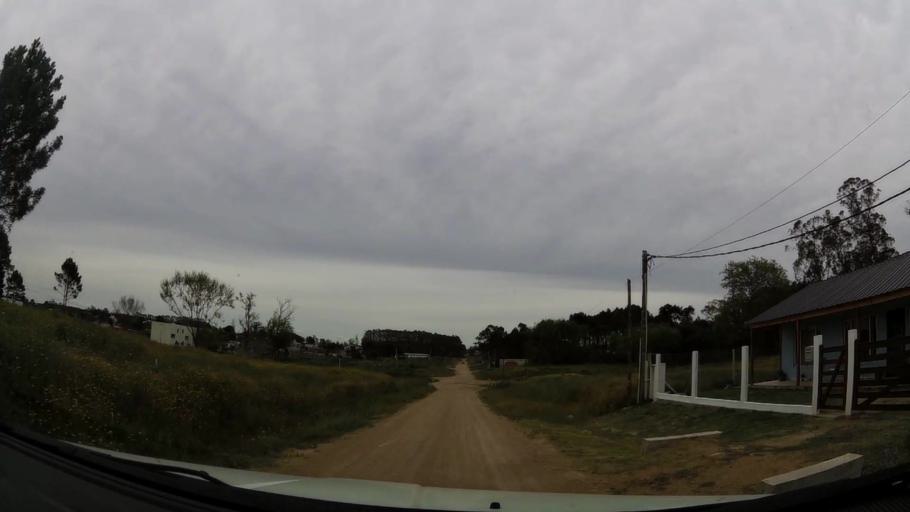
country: UY
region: Maldonado
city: Maldonado
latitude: -34.8969
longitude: -54.9888
